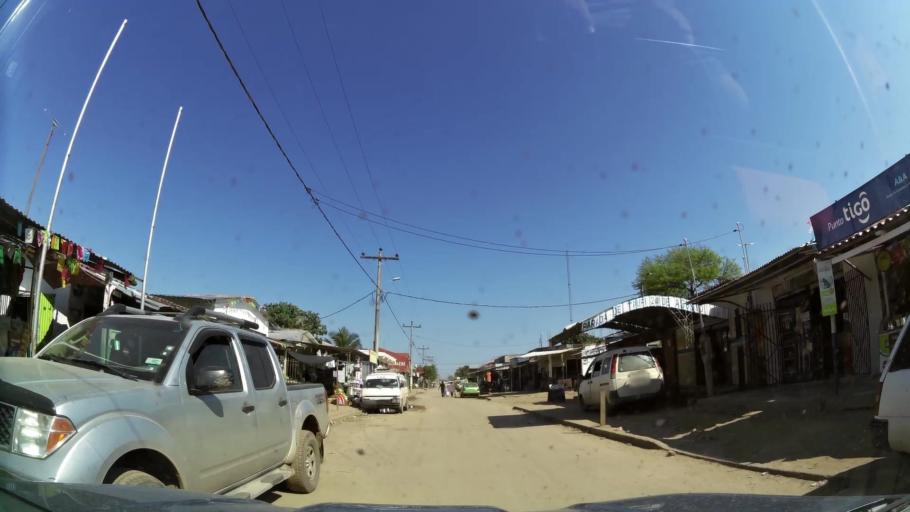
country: BO
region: Santa Cruz
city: Cotoca
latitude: -17.7399
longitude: -63.0741
